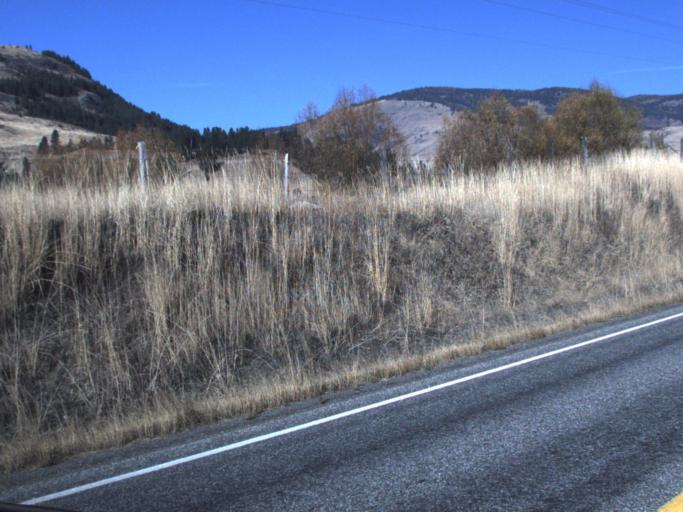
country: CA
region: British Columbia
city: Grand Forks
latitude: 48.8646
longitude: -118.6054
